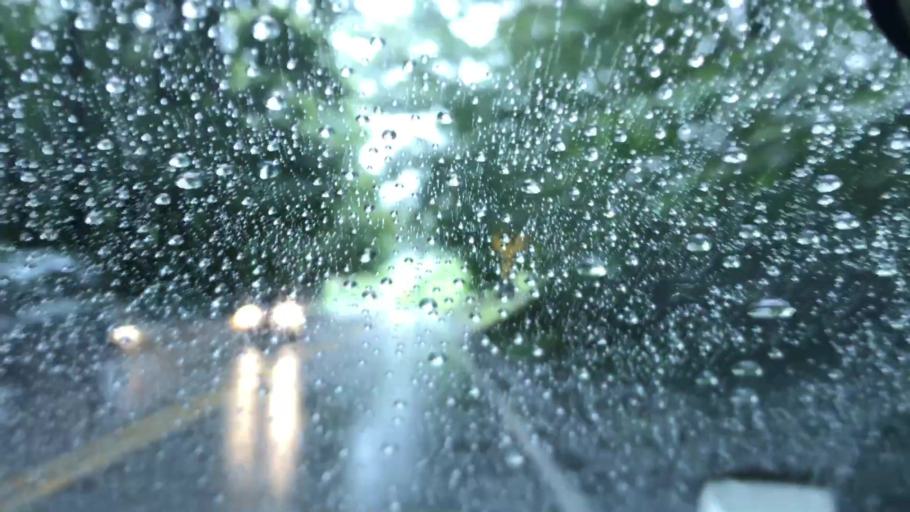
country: US
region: Pennsylvania
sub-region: Allegheny County
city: Allison Park
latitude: 40.5526
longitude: -79.9721
